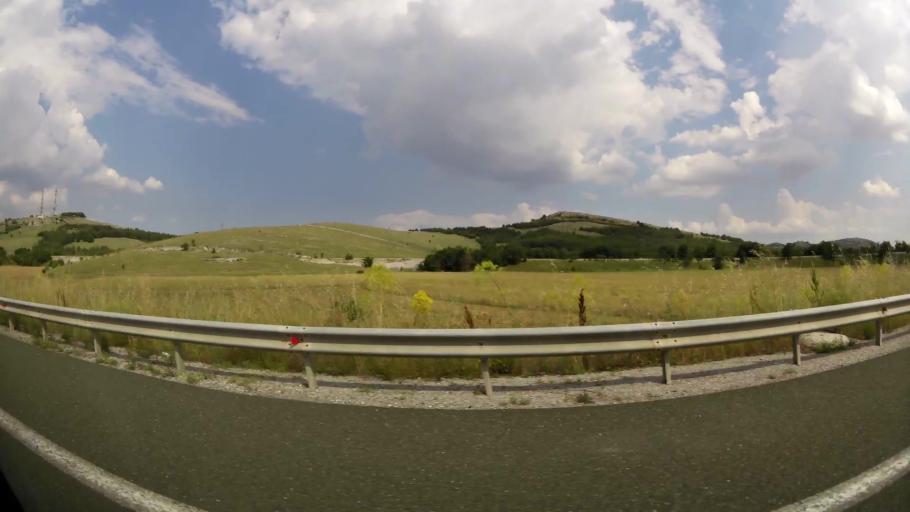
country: GR
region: West Macedonia
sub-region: Nomos Kozanis
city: Koila
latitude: 40.3534
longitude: 21.8112
